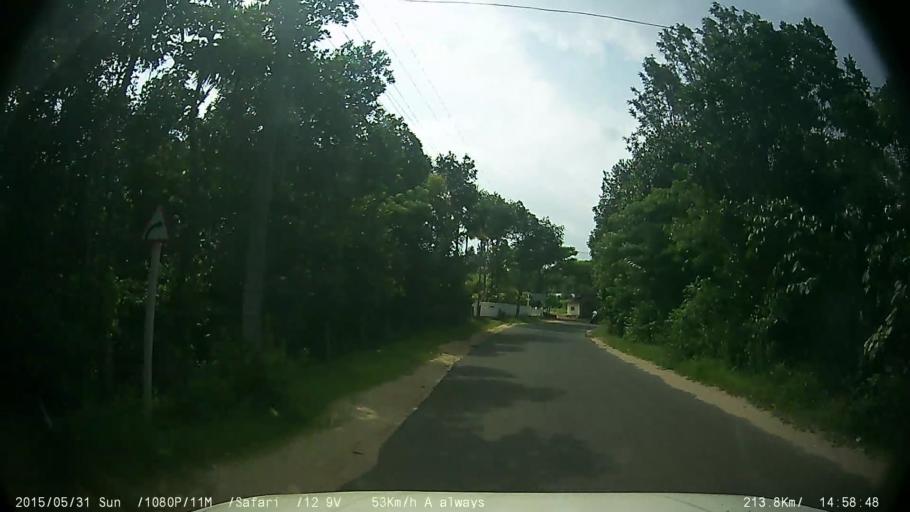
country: IN
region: Kerala
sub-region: Wayanad
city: Kalpetta
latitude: 11.6069
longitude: 76.2079
